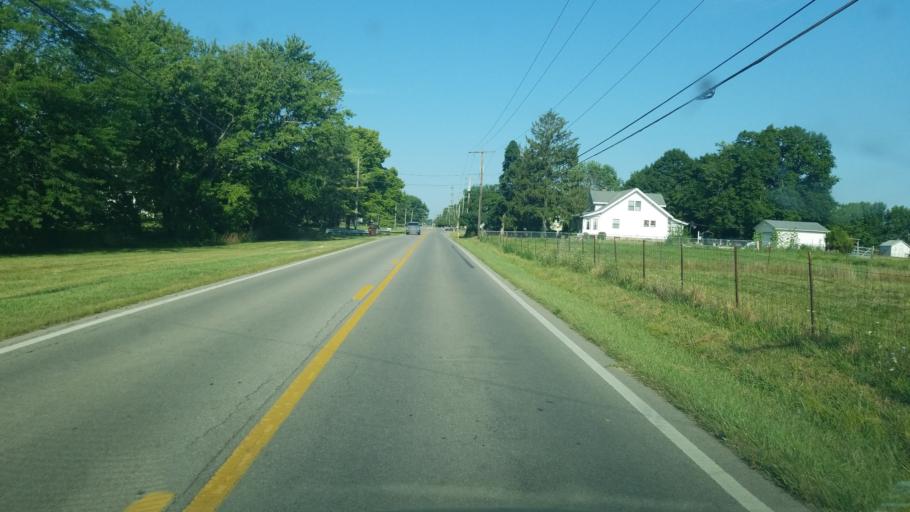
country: US
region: Ohio
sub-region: Franklin County
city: Grove City
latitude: 39.8823
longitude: -83.1120
